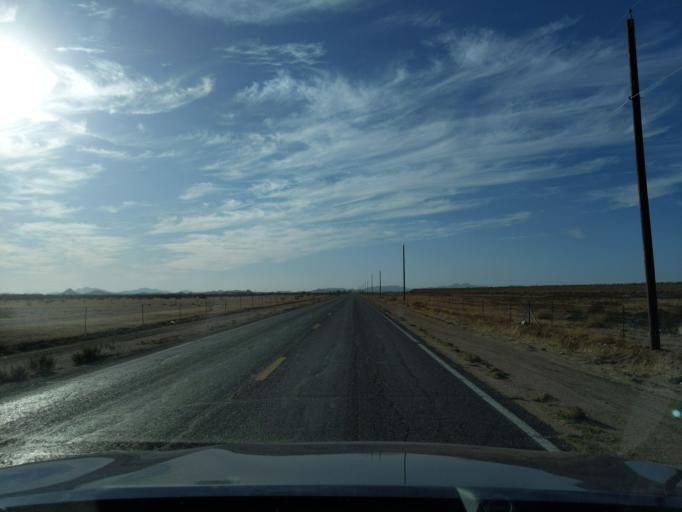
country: US
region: Arizona
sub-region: Pinal County
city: Florence
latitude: 33.1183
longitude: -111.3909
